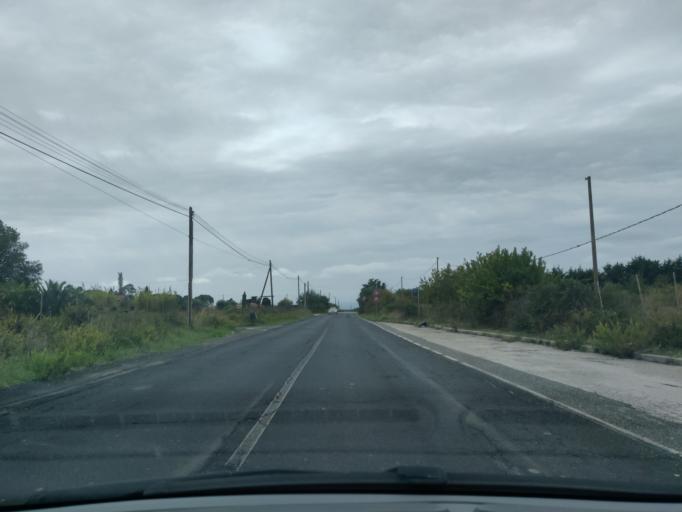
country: IT
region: Latium
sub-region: Citta metropolitana di Roma Capitale
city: Civitavecchia
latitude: 42.1070
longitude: 11.8307
